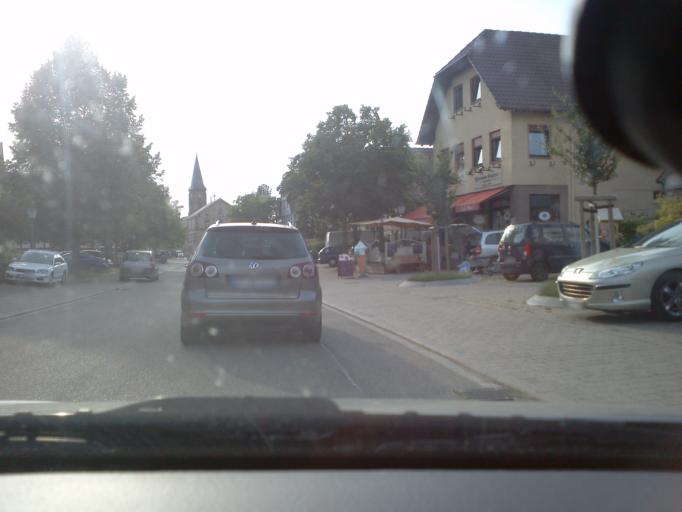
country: DE
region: Baden-Wuerttemberg
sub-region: Karlsruhe Region
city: Olbronn-Durrn
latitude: 48.9809
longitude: 8.7532
